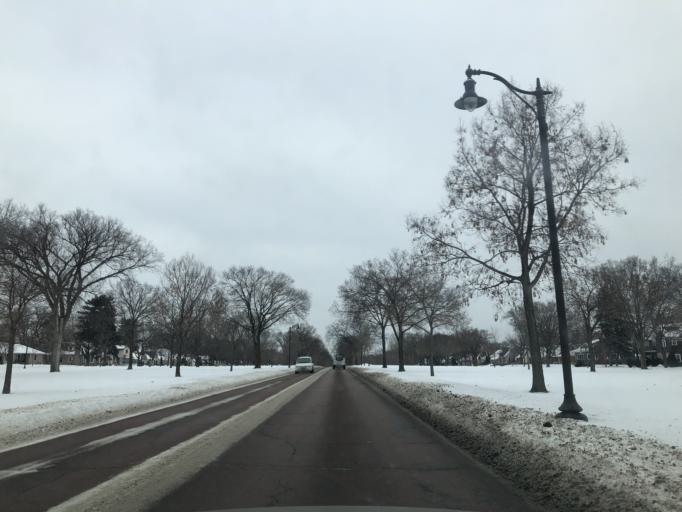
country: US
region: Minnesota
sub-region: Hennepin County
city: Robbinsdale
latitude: 45.0246
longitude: -93.3192
